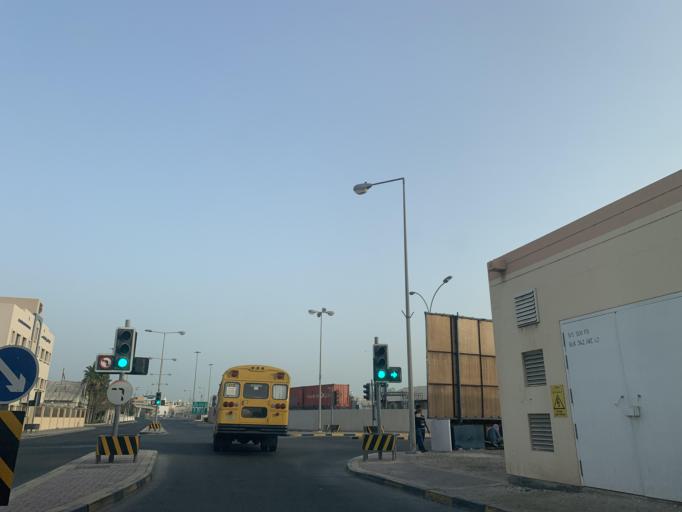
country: BH
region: Manama
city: Manama
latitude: 26.2002
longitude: 50.6039
